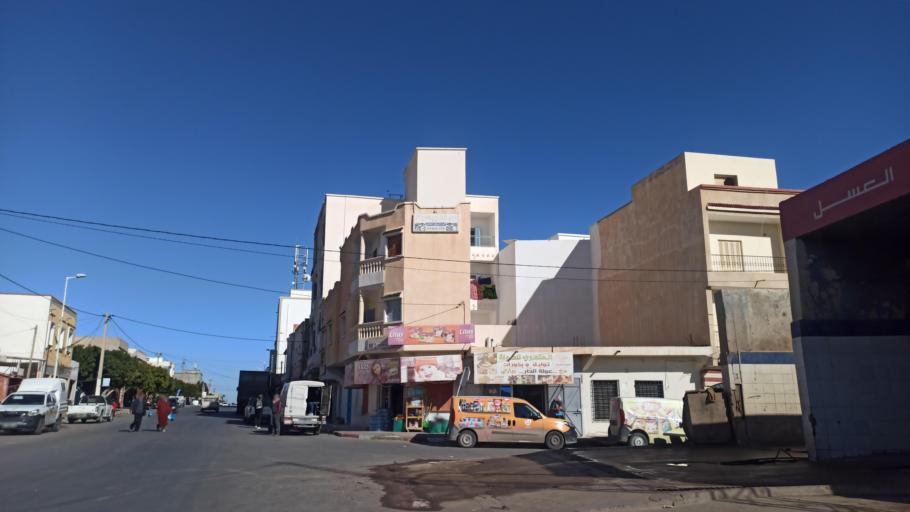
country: TN
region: Sidi Bu Zayd
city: Bi'r al Hufayy
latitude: 34.9327
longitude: 9.1965
